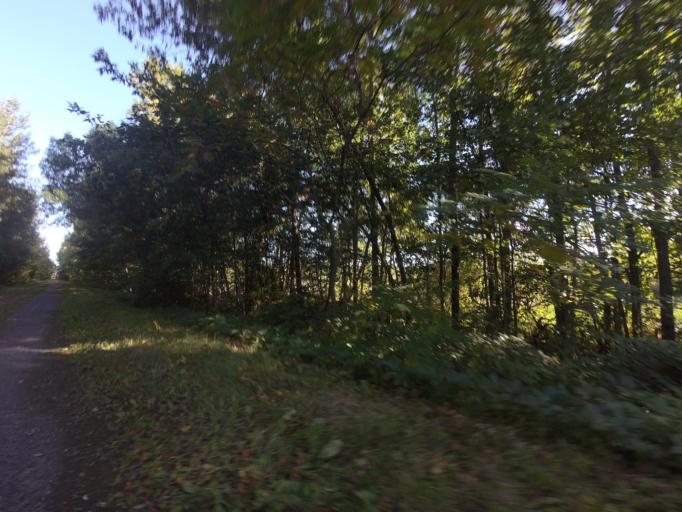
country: CA
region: Ontario
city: Hawkesbury
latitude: 45.5266
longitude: -74.5529
